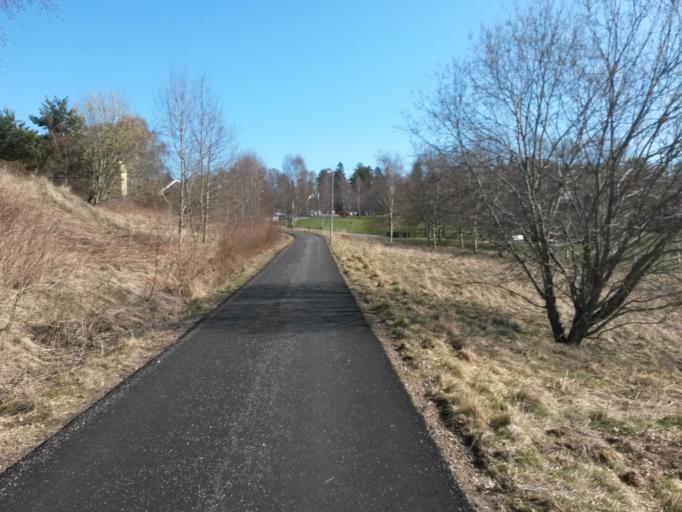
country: SE
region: Vaestra Goetaland
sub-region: Vargarda Kommun
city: Vargarda
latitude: 58.0283
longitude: 12.7960
